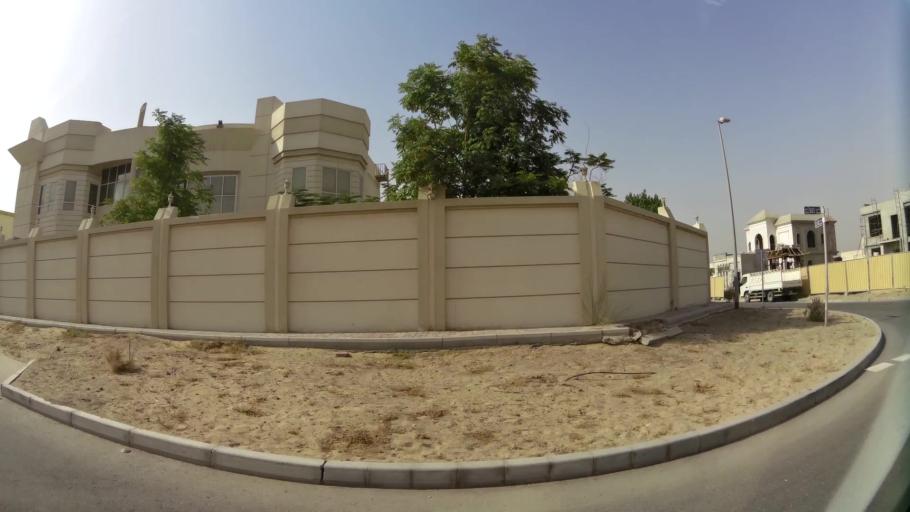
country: AE
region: Ash Shariqah
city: Sharjah
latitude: 25.2527
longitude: 55.4518
